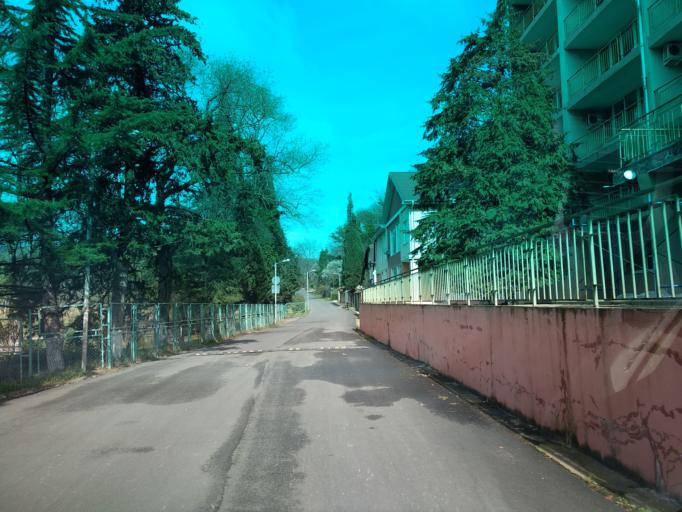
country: RU
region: Krasnodarskiy
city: Shepsi
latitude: 44.0334
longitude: 39.1469
